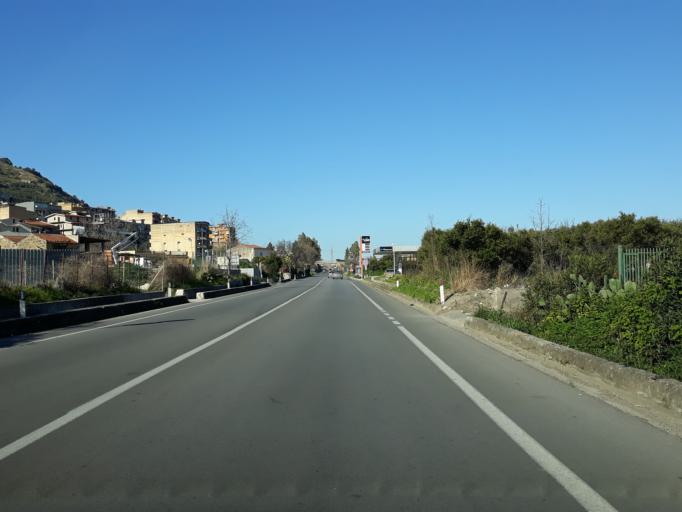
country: IT
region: Sicily
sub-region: Palermo
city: Misilmeri
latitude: 38.0318
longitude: 13.4573
